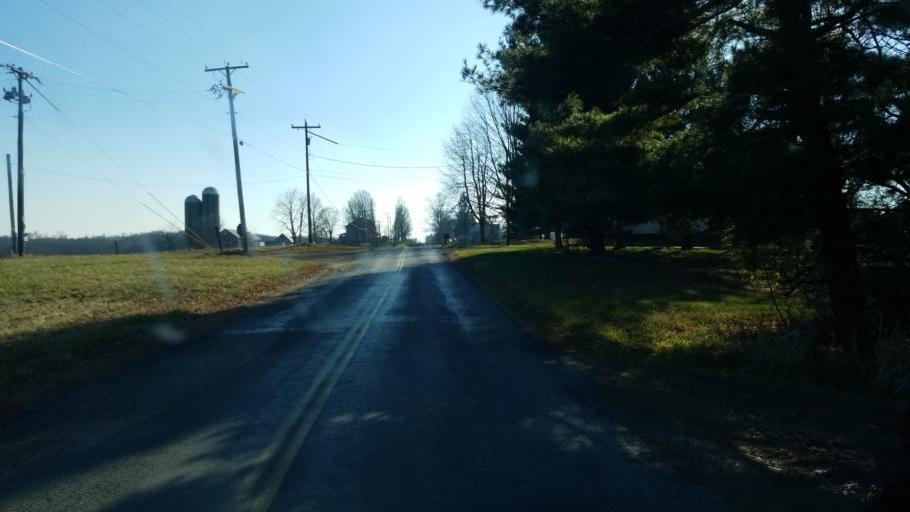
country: US
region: Ohio
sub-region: Portage County
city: Mantua
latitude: 41.3225
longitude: -81.2627
